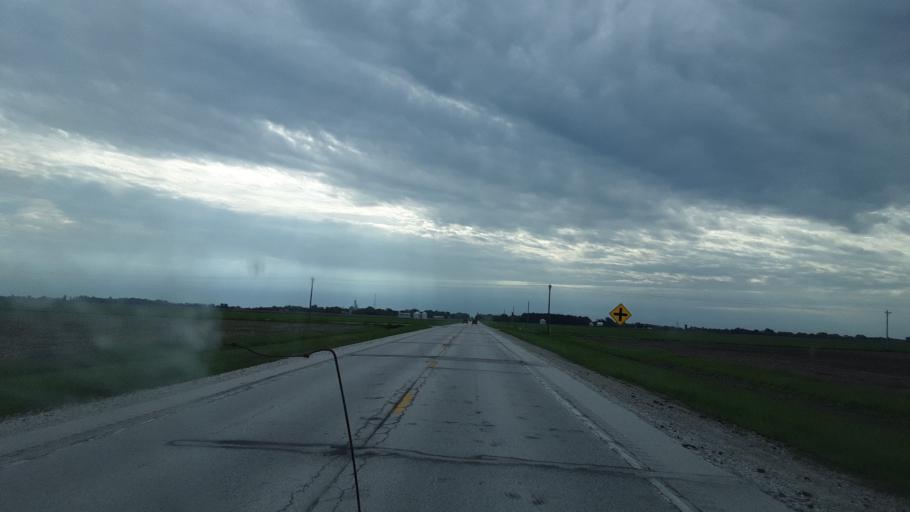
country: US
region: Illinois
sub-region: Hancock County
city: Hamilton
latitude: 40.3953
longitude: -91.2743
